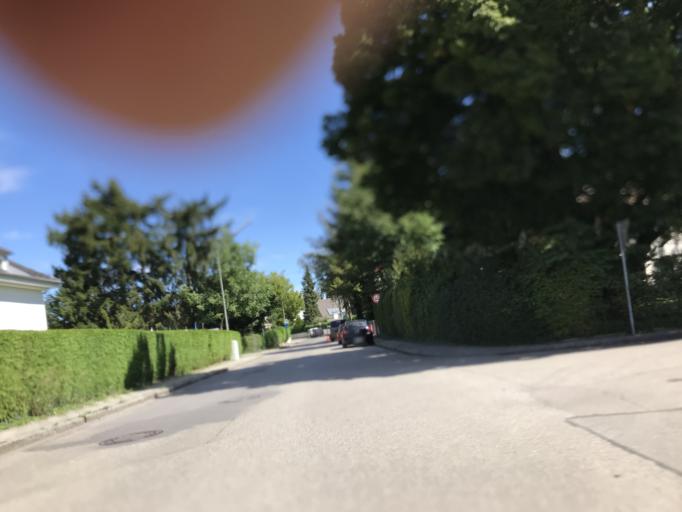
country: DE
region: Bavaria
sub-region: Upper Bavaria
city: Grobenzell
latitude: 48.1855
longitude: 11.3624
